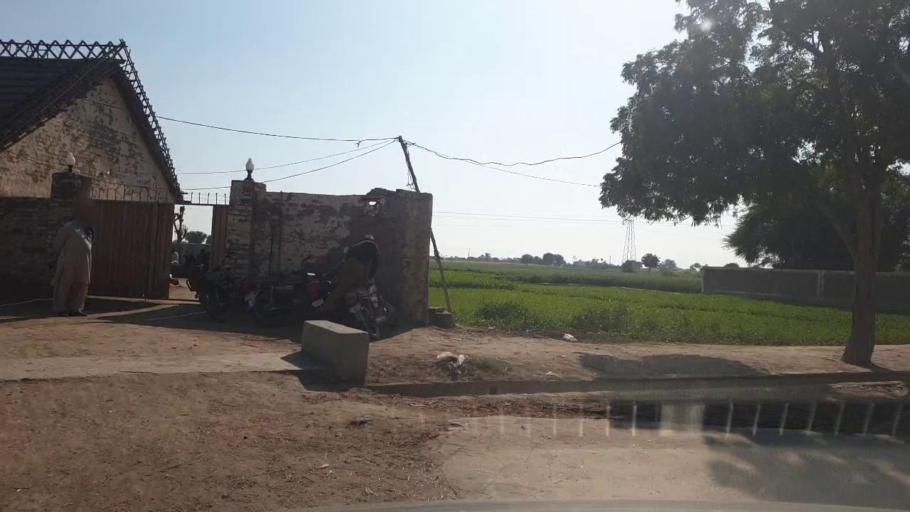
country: PK
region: Sindh
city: Shahpur Chakar
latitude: 26.1457
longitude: 68.6758
